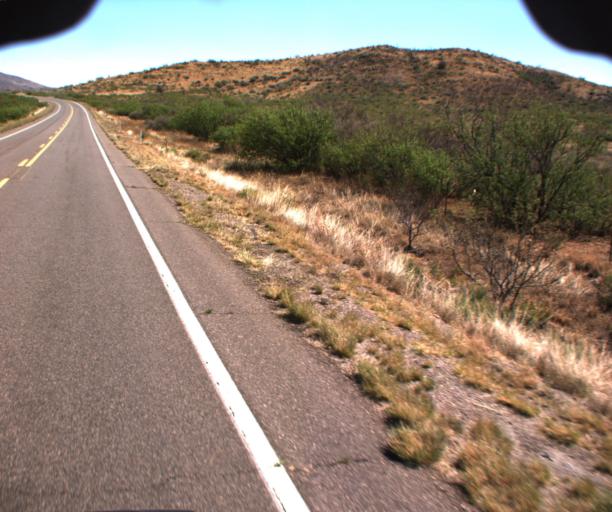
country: US
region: Arizona
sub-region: Cochise County
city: Douglas
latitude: 31.4819
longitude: -109.4430
